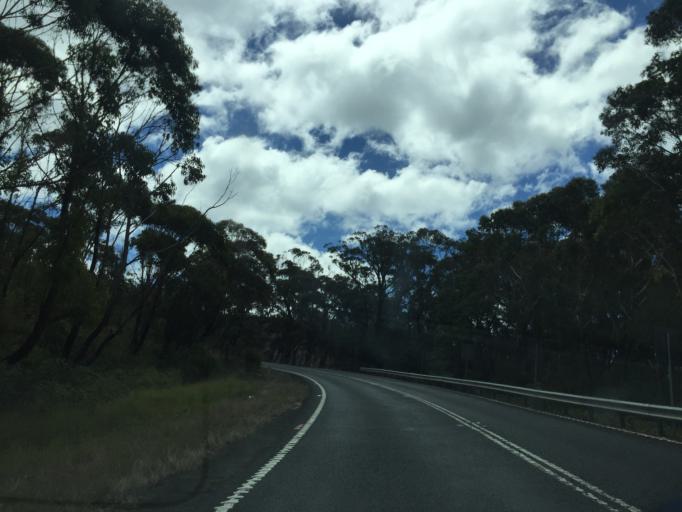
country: AU
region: New South Wales
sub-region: Blue Mountains Municipality
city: Blackheath
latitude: -33.5549
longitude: 150.3428
